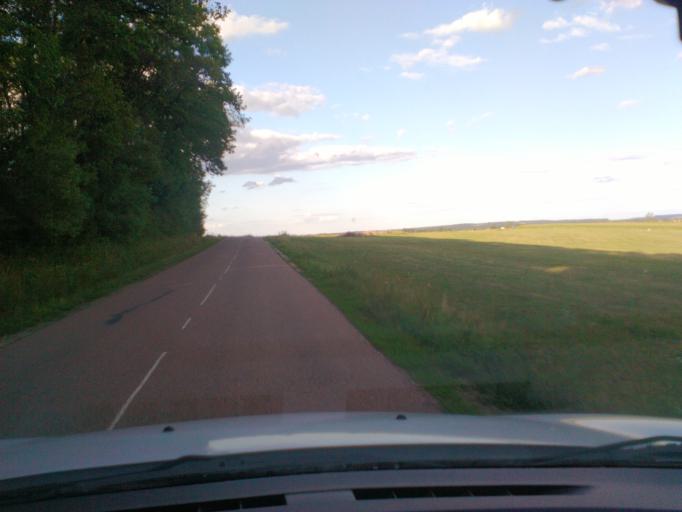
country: FR
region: Lorraine
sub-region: Departement des Vosges
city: Mirecourt
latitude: 48.3497
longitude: 6.0403
